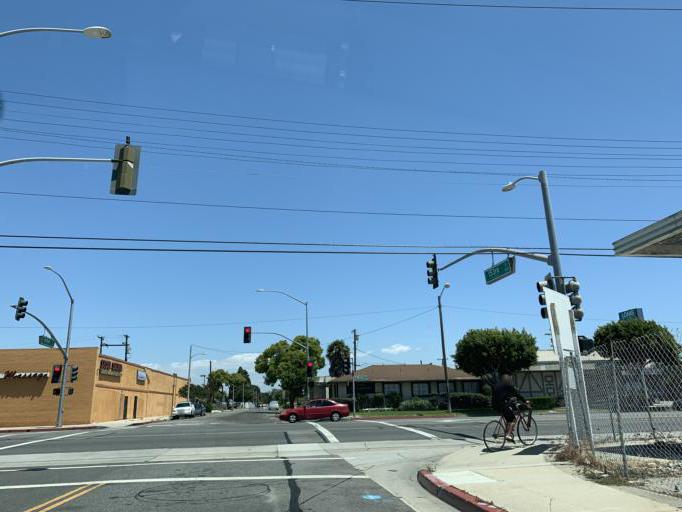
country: US
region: California
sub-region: Los Angeles County
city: Gardena
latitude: 33.8928
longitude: -118.3095
